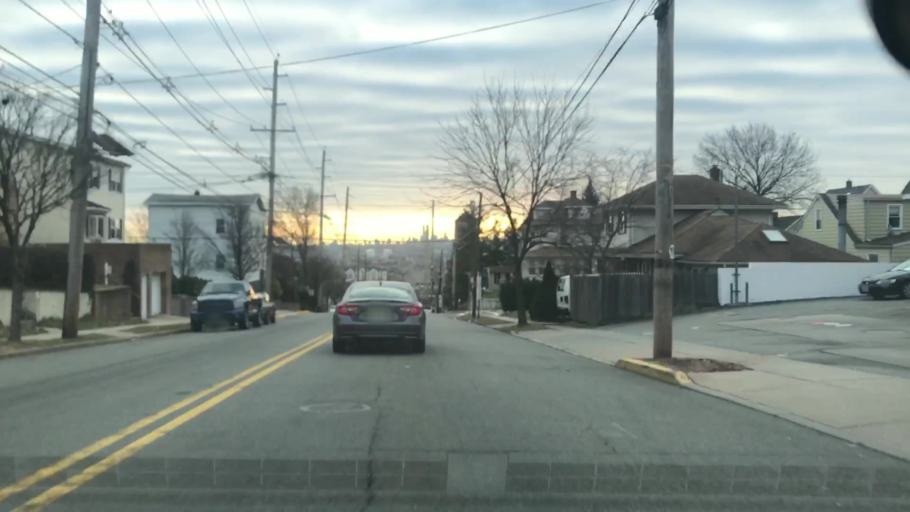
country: US
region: New Jersey
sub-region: Bergen County
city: East Rutherford
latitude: 40.8367
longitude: -74.0945
